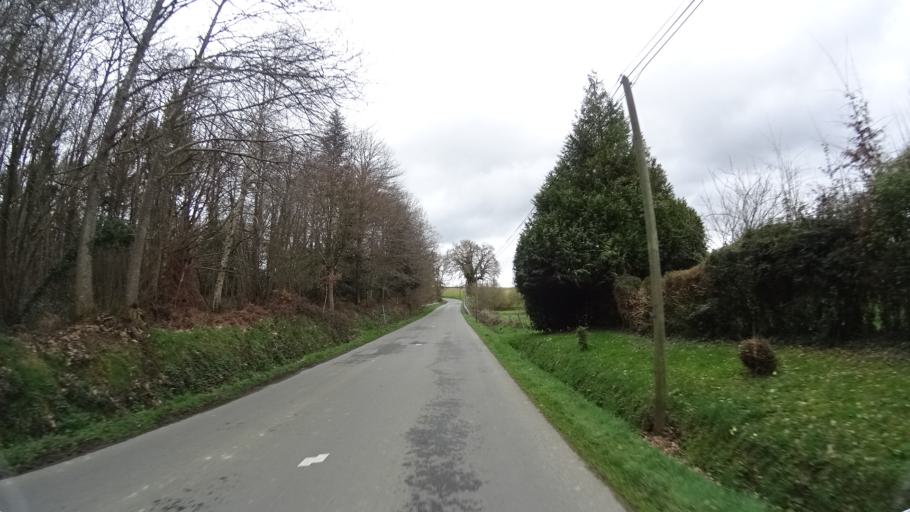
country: FR
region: Brittany
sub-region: Departement d'Ille-et-Vilaine
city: Saint-Gilles
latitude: 48.1791
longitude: -1.8314
